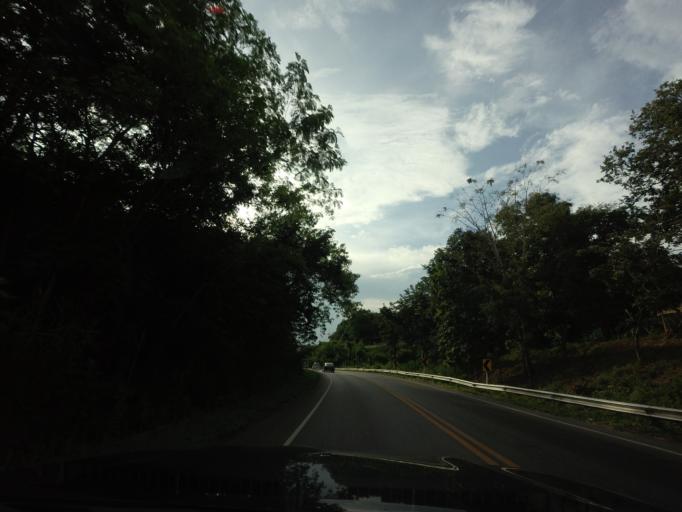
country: TH
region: Nong Khai
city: Pho Tak
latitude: 17.8034
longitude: 102.3194
